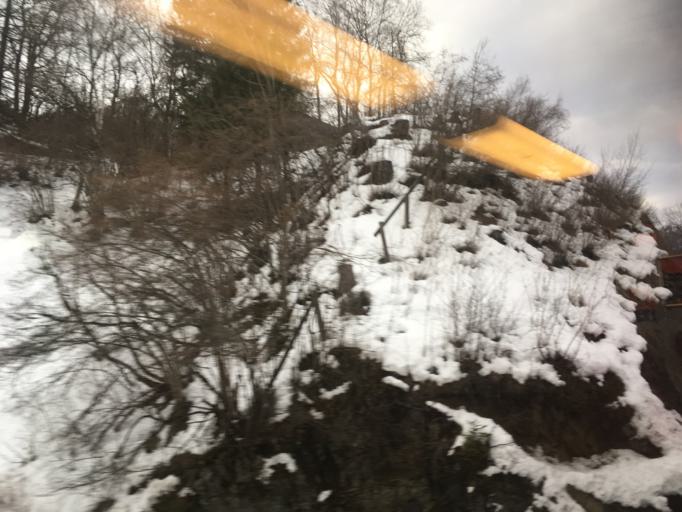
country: CH
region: Grisons
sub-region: Albula District
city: Tiefencastel
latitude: 46.6753
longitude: 9.6770
